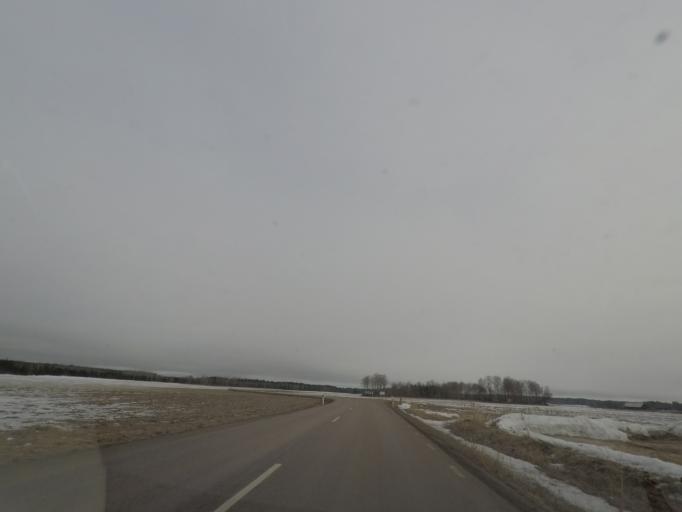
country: SE
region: Vaestmanland
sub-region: Vasteras
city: Skultuna
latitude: 59.7305
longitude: 16.4176
